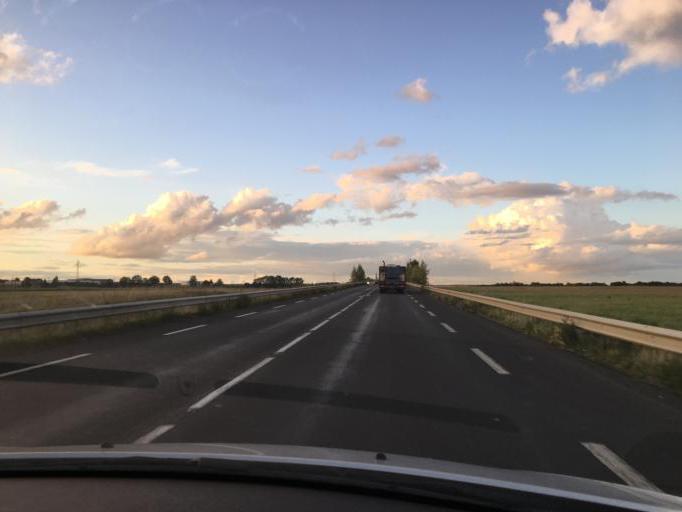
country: FR
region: Centre
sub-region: Departement d'Eure-et-Loir
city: Chateaudun
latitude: 48.0780
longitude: 1.3615
